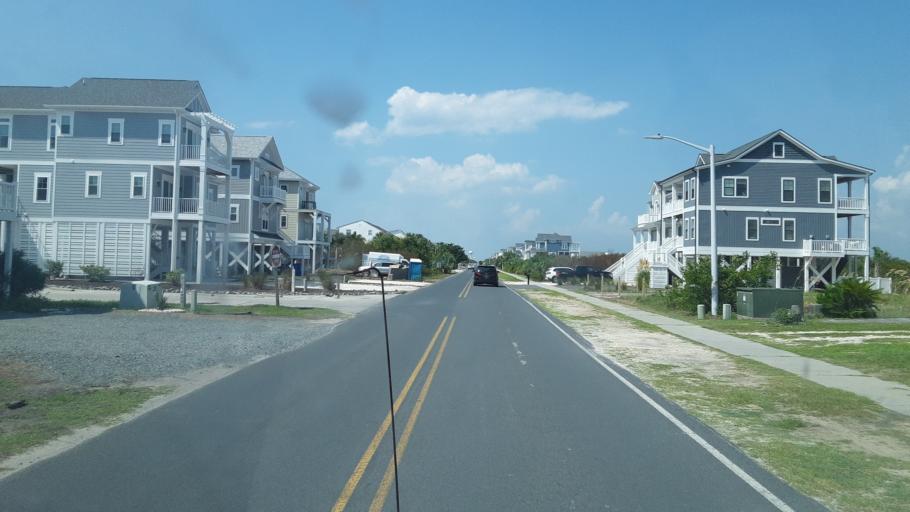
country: US
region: North Carolina
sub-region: Brunswick County
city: Shallotte
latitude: 33.8955
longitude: -78.4085
